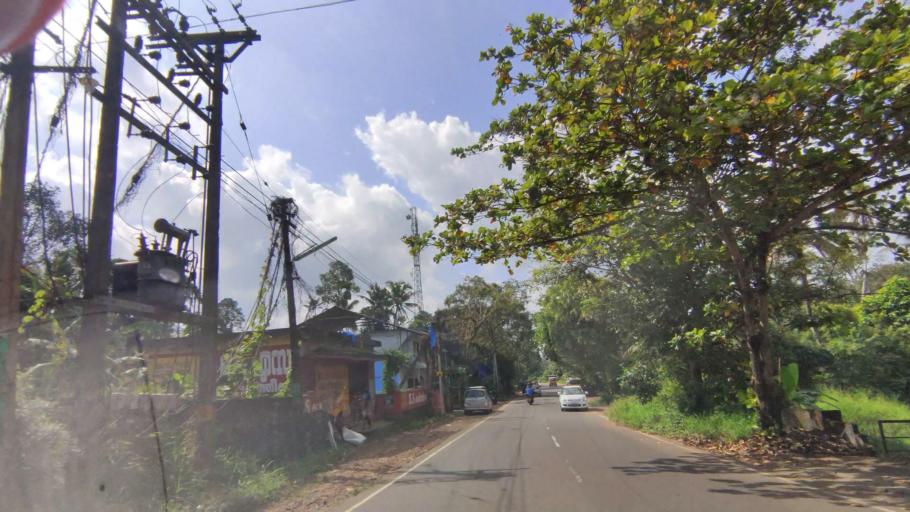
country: IN
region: Kerala
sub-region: Kottayam
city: Kottayam
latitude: 9.6716
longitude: 76.5545
